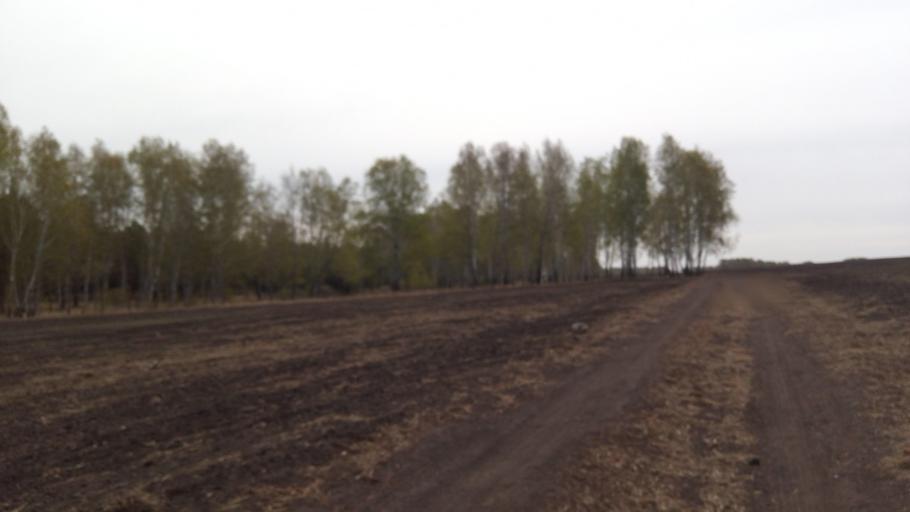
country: RU
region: Chelyabinsk
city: Timiryazevskiy
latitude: 55.0206
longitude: 60.8525
